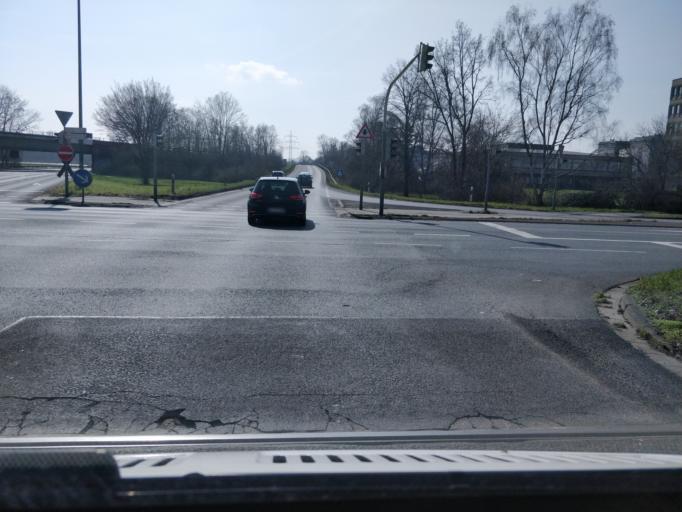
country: DE
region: North Rhine-Westphalia
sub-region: Regierungsbezirk Dusseldorf
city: Neuss
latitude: 51.1991
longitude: 6.7172
